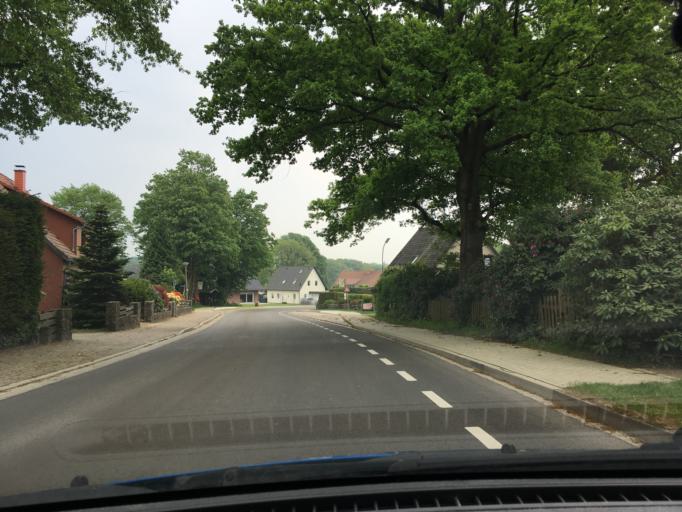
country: DE
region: Lower Saxony
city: Seevetal
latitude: 53.4082
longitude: 9.8969
